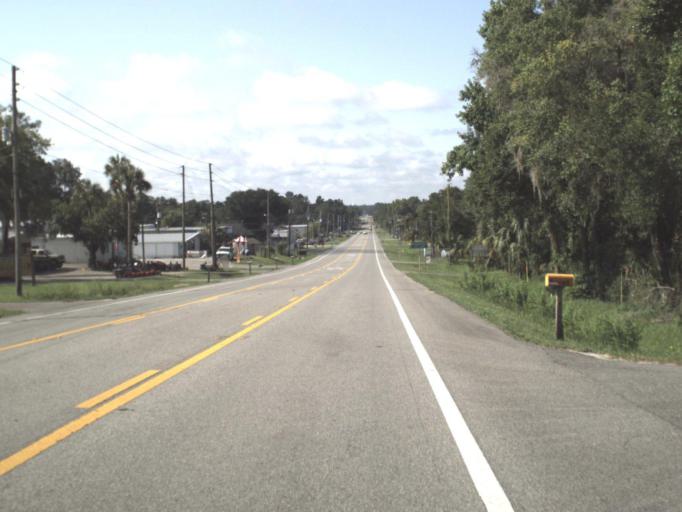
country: US
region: Florida
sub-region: Hernando County
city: North Brooksville
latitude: 28.5714
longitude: -82.3978
